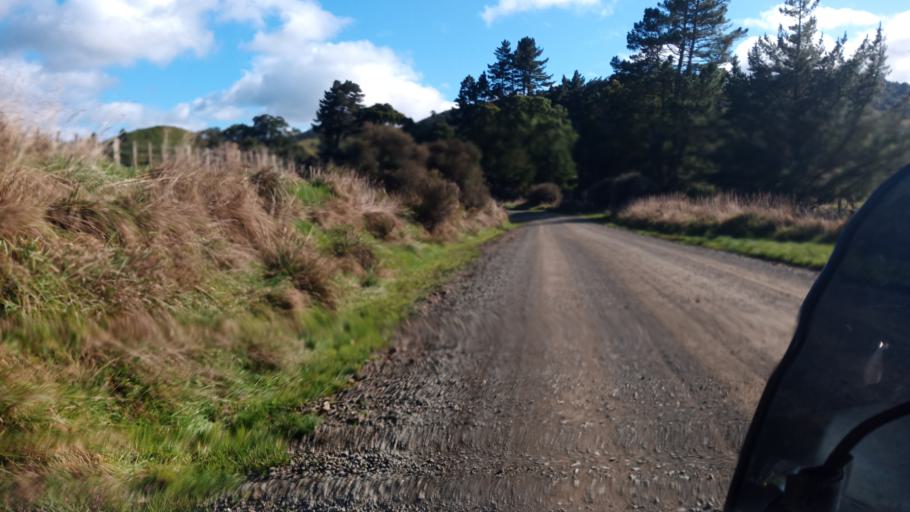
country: NZ
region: Bay of Plenty
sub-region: Opotiki District
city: Opotiki
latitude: -38.4646
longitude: 177.4269
